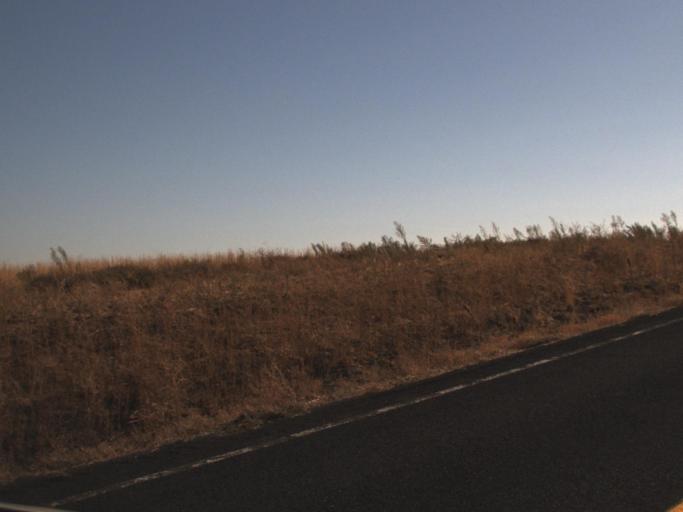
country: US
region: Washington
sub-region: Adams County
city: Ritzville
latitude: 47.0195
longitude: -118.6636
